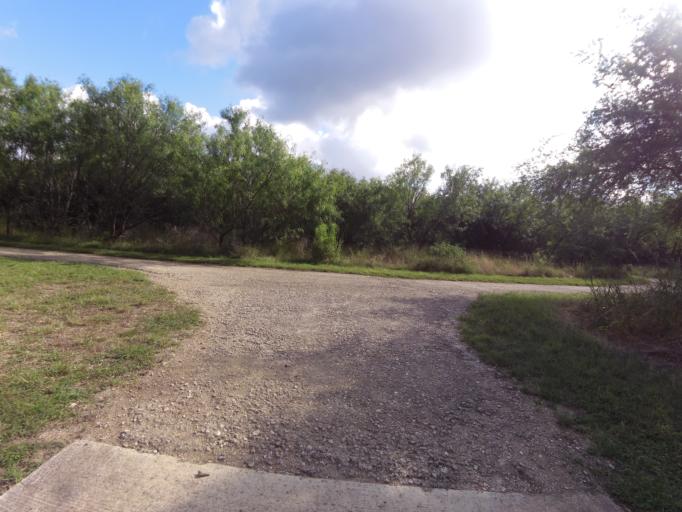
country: US
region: Texas
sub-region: Bexar County
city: Helotes
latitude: 29.5583
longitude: -98.6292
